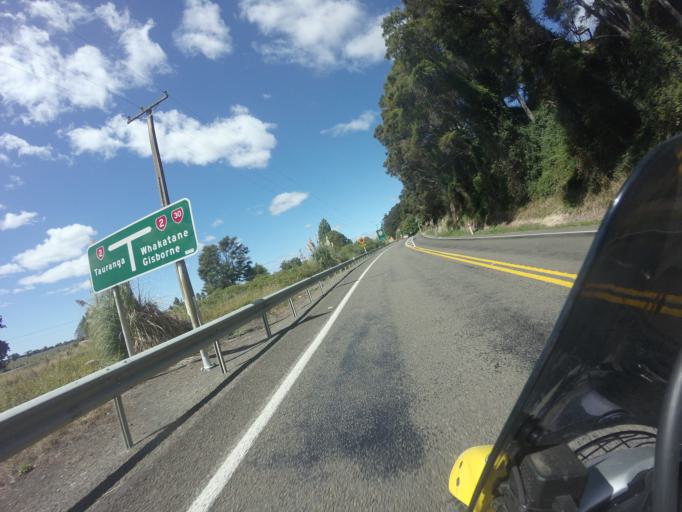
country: NZ
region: Bay of Plenty
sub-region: Whakatane District
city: Edgecumbe
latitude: -37.9976
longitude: 176.8845
